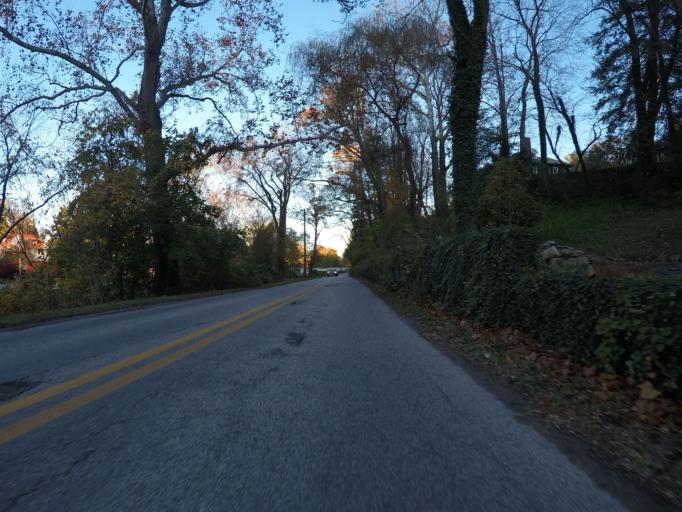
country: US
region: West Virginia
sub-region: Cabell County
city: Huntington
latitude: 38.4063
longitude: -82.4438
